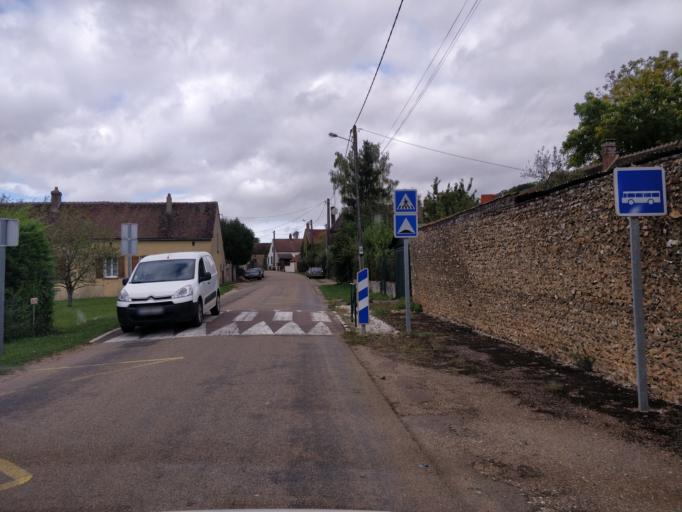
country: FR
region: Champagne-Ardenne
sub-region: Departement de l'Aube
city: Aix-en-Othe
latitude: 48.1680
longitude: 3.6279
